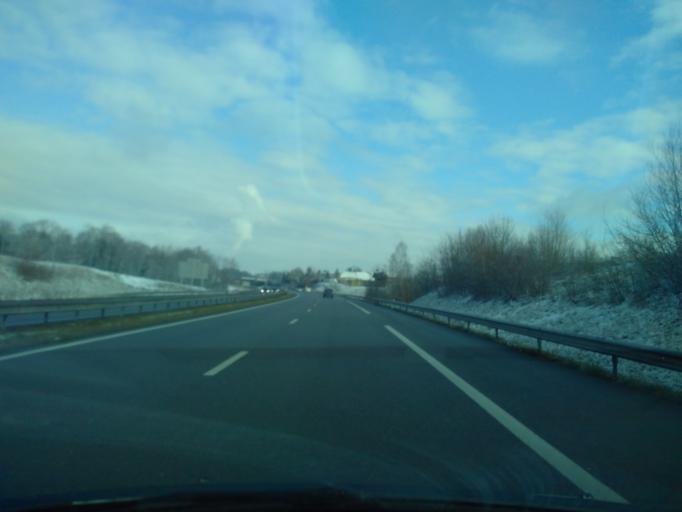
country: FR
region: Rhone-Alpes
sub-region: Departement de la Haute-Savoie
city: Viuz-la-Chiesaz
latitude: 45.8390
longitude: 6.0547
